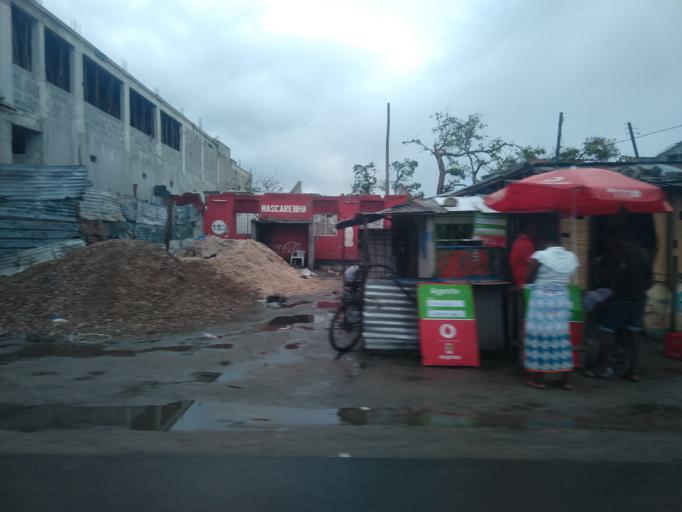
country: MZ
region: Sofala
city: Beira
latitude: -19.7899
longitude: 34.8860
